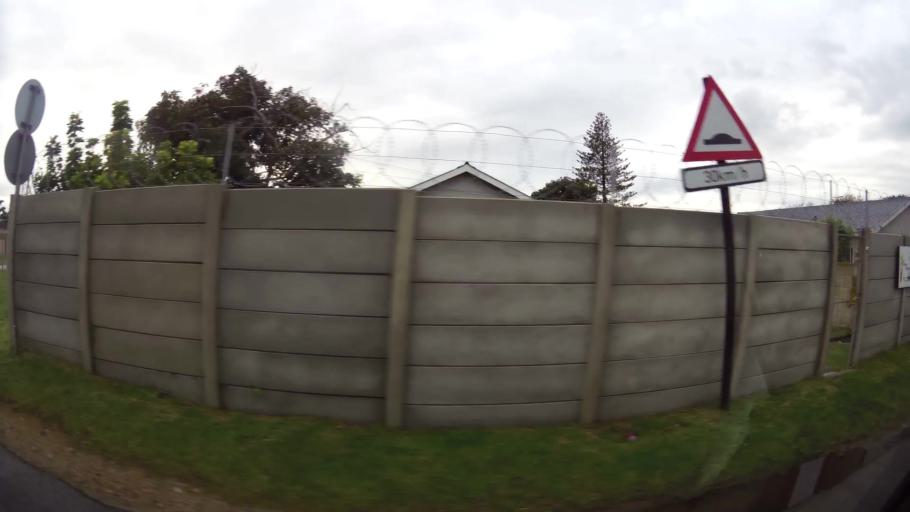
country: ZA
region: Eastern Cape
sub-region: Nelson Mandela Bay Metropolitan Municipality
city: Port Elizabeth
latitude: -33.9966
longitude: 25.5287
